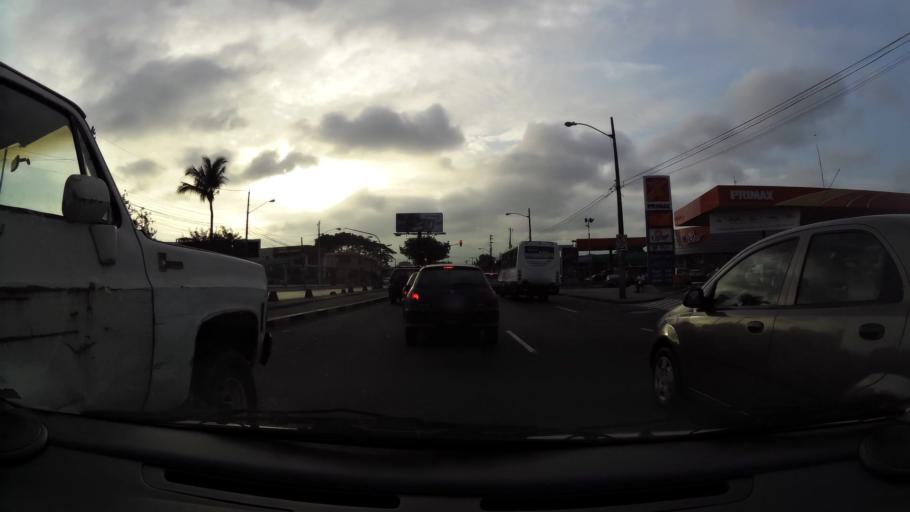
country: EC
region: Guayas
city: Eloy Alfaro
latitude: -2.1712
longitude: -79.8905
